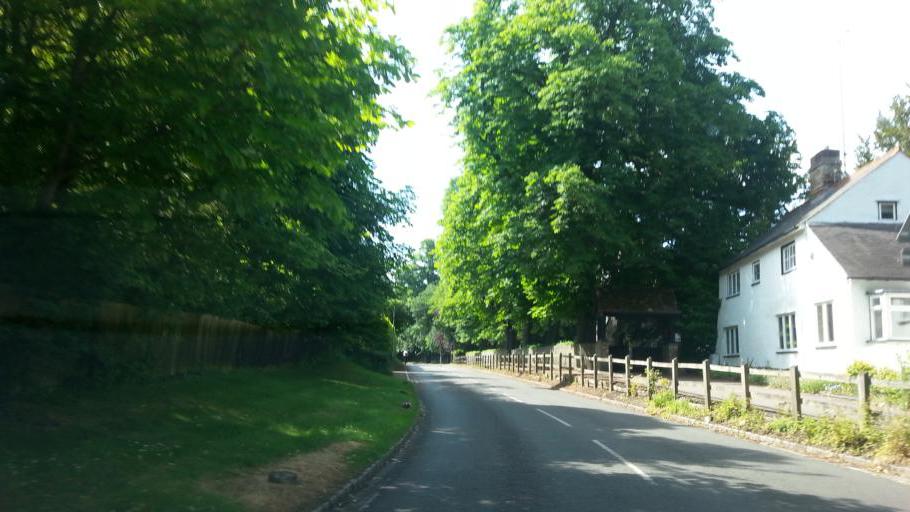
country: GB
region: England
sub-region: Cambridgeshire
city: Sawston
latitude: 52.1472
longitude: 0.1492
